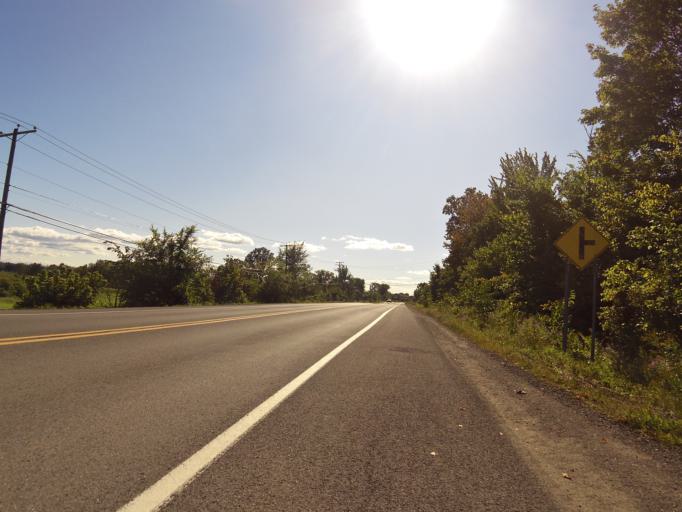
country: CA
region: Ontario
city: Clarence-Rockland
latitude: 45.5276
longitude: -75.4782
